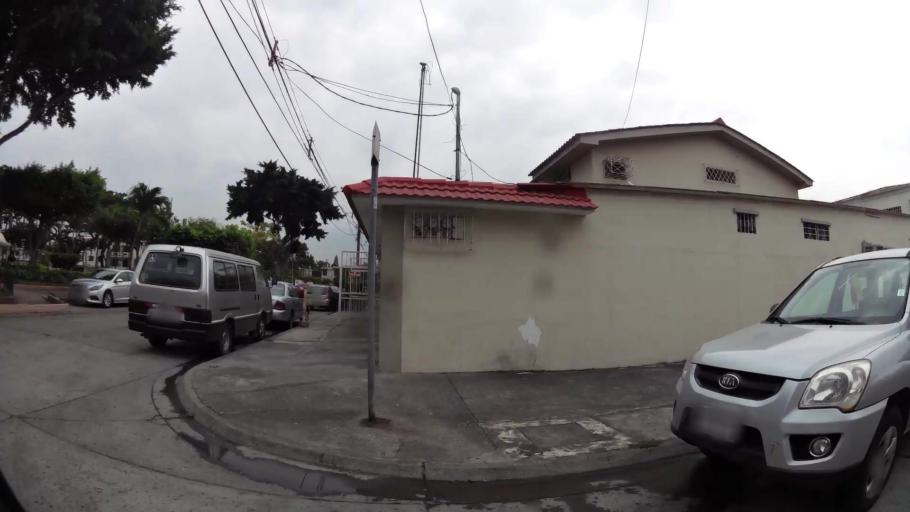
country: EC
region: Guayas
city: Eloy Alfaro
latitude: -2.1457
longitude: -79.8920
